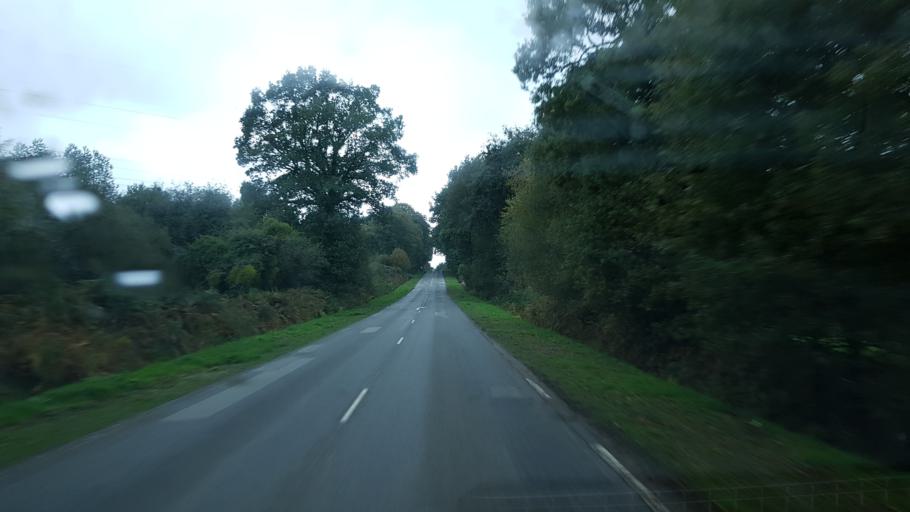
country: FR
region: Brittany
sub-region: Departement du Morbihan
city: Elven
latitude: 47.7441
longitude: -2.5697
